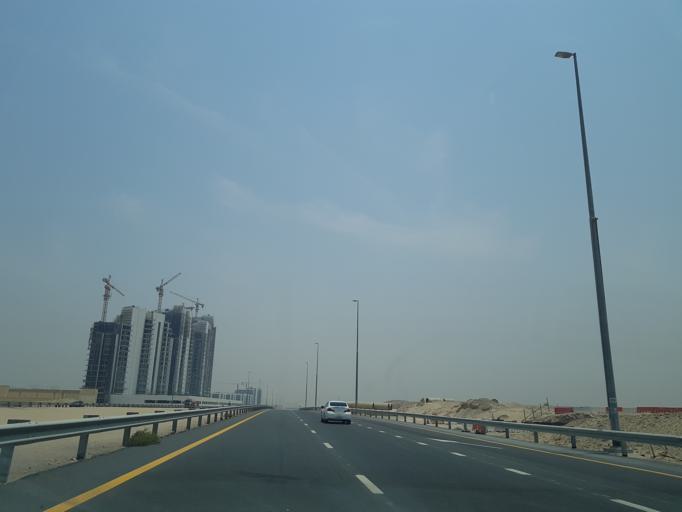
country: AE
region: Dubai
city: Dubai
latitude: 25.0223
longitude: 55.2411
